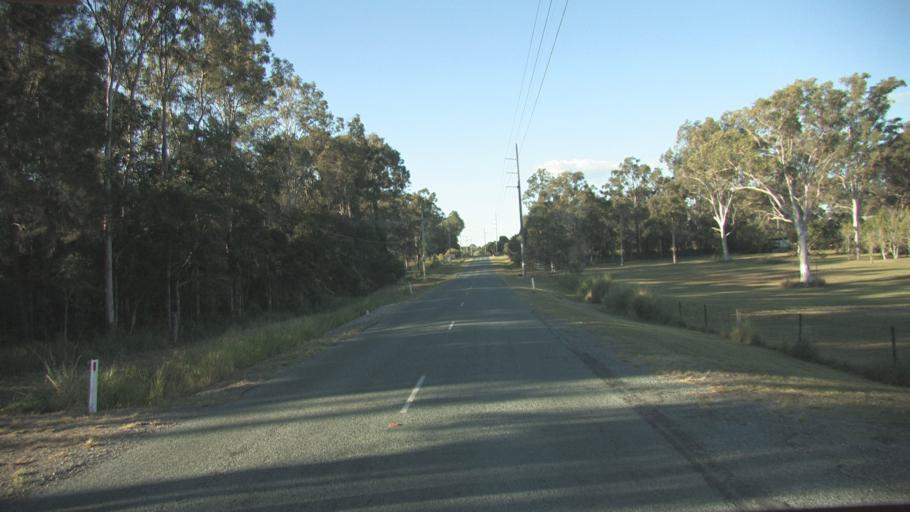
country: AU
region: Queensland
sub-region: Logan
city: Logan Reserve
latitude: -27.7319
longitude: 153.0924
